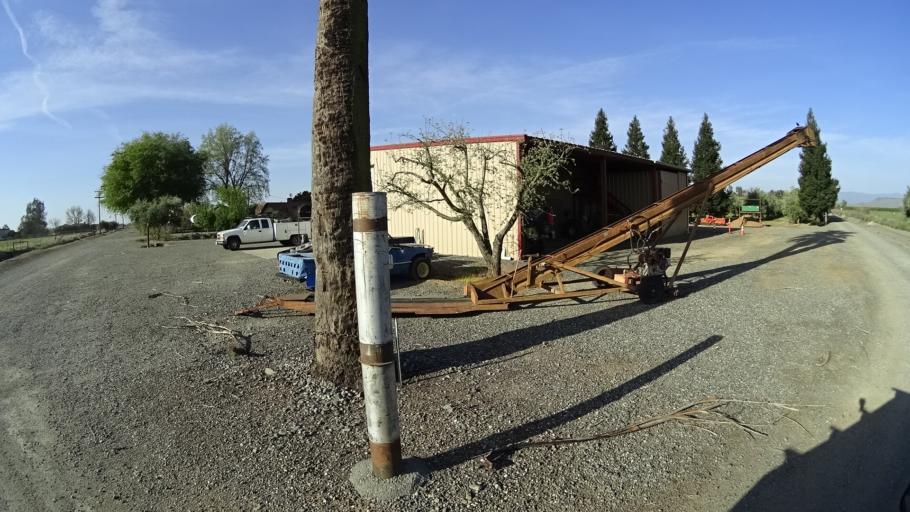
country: US
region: California
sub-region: Glenn County
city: Orland
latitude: 39.7333
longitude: -122.2343
